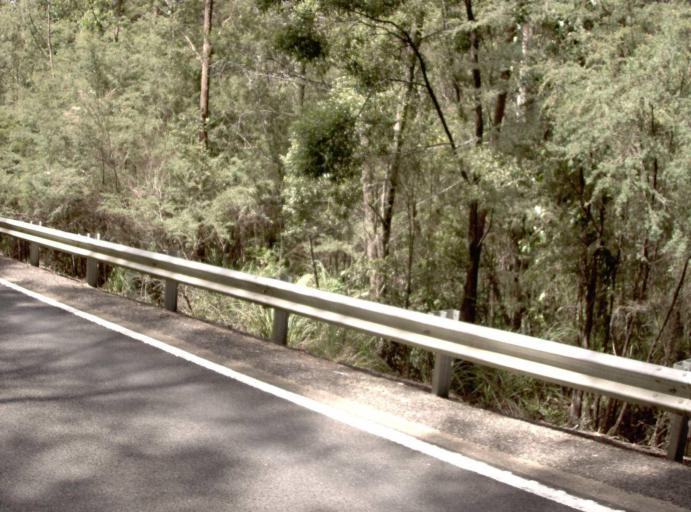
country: AU
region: New South Wales
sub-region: Bombala
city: Bombala
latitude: -37.5425
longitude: 149.3680
